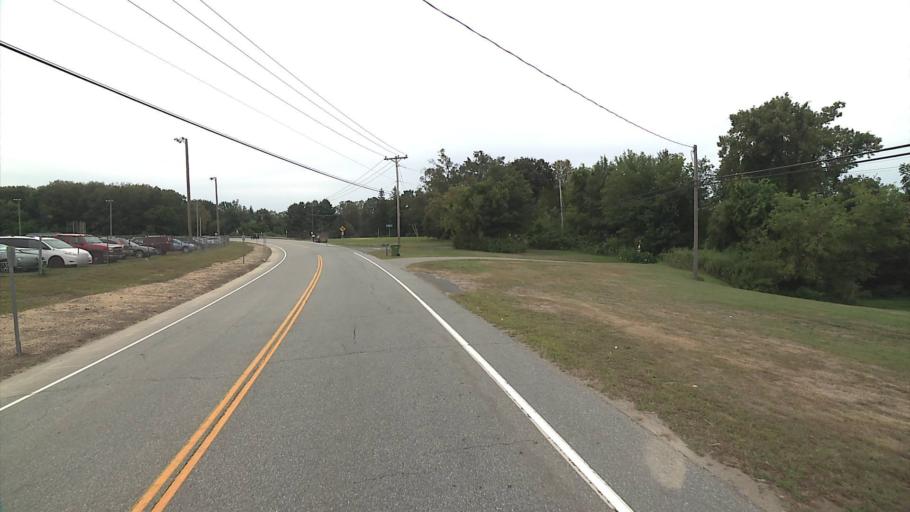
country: US
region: Connecticut
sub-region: Tolland County
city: Hebron
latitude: 41.6758
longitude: -72.4101
